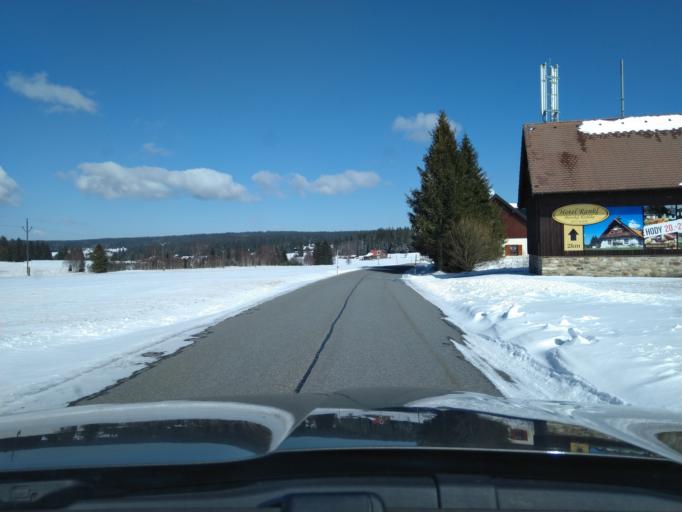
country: CZ
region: Jihocesky
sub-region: Okres Prachatice
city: Borova Lada
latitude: 49.0449
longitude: 13.5779
